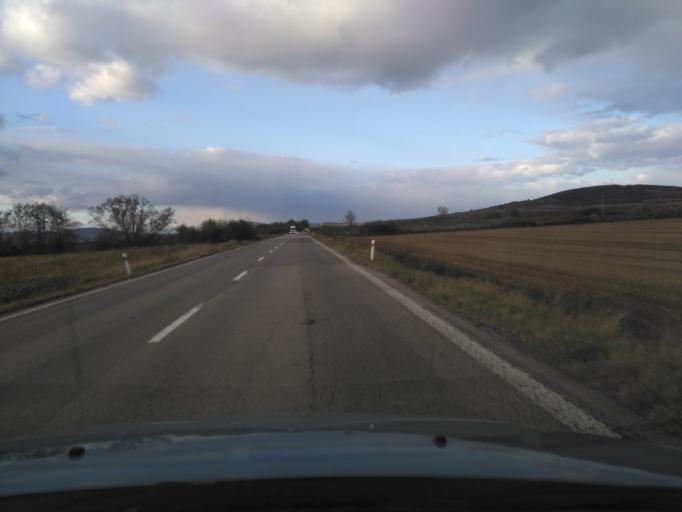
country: HU
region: Borsod-Abauj-Zemplen
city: Satoraljaujhely
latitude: 48.4393
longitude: 21.6555
